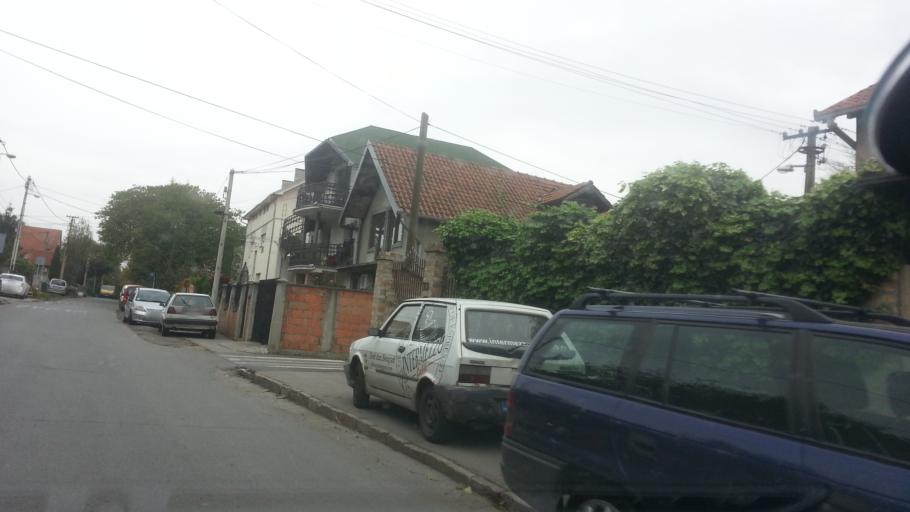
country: RS
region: Central Serbia
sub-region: Belgrade
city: Zemun
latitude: 44.8374
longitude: 20.3962
